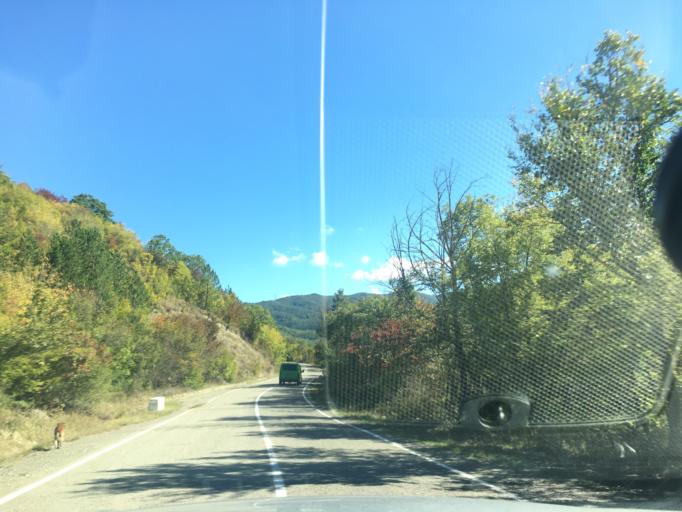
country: GE
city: Didi Lilo
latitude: 41.8547
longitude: 44.8949
